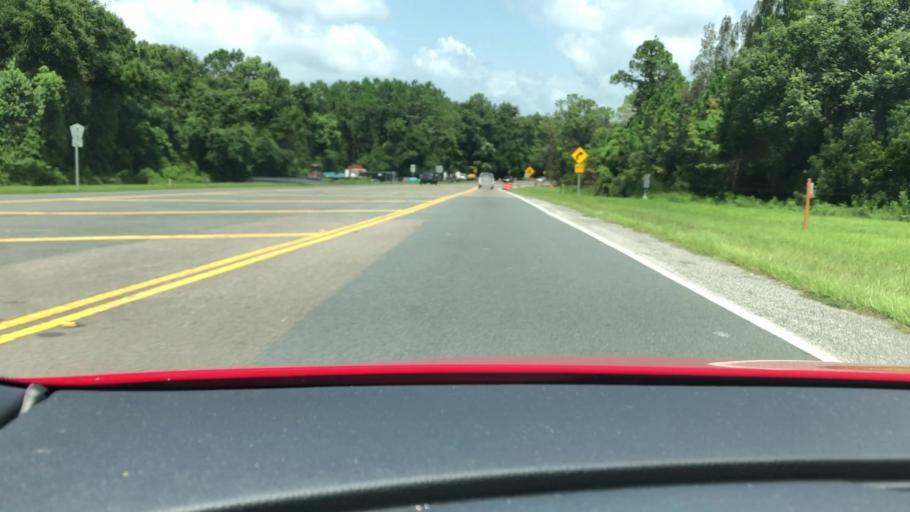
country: US
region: Florida
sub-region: Volusia County
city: Lake Helen
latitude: 29.0163
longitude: -81.2486
